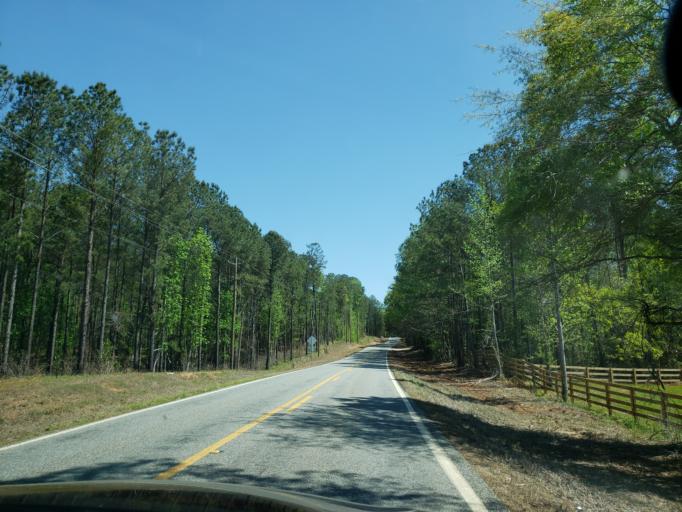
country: US
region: Alabama
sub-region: Elmore County
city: Tallassee
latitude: 32.6848
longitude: -85.8697
